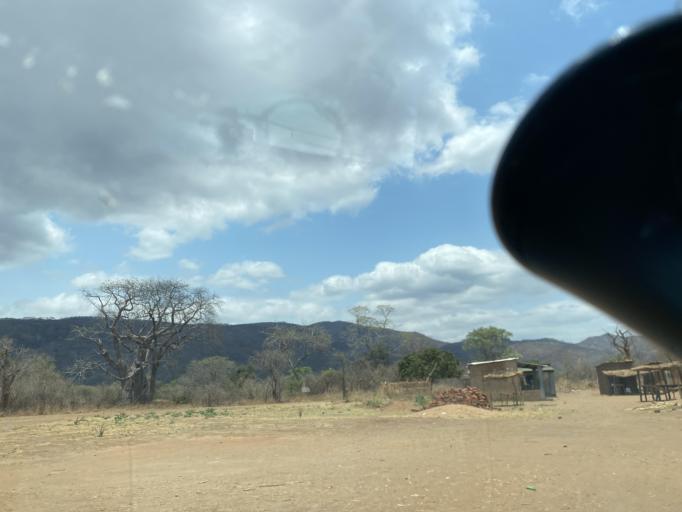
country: ZM
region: Lusaka
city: Luangwa
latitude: -15.1866
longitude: 29.7308
